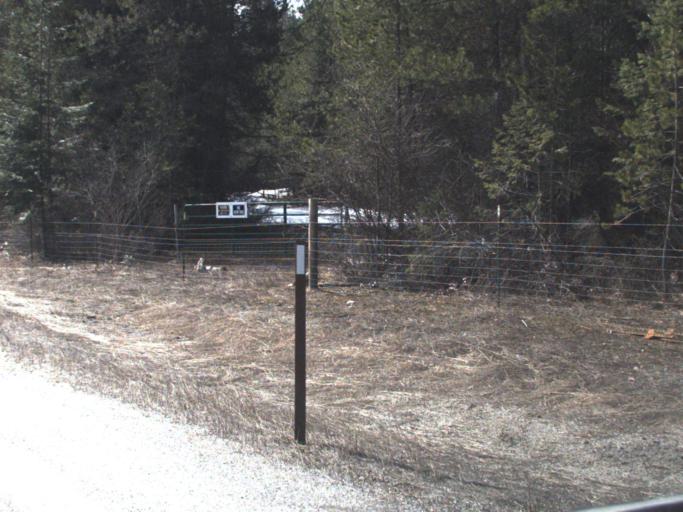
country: US
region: Washington
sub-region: Stevens County
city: Chewelah
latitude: 48.6302
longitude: -117.3689
